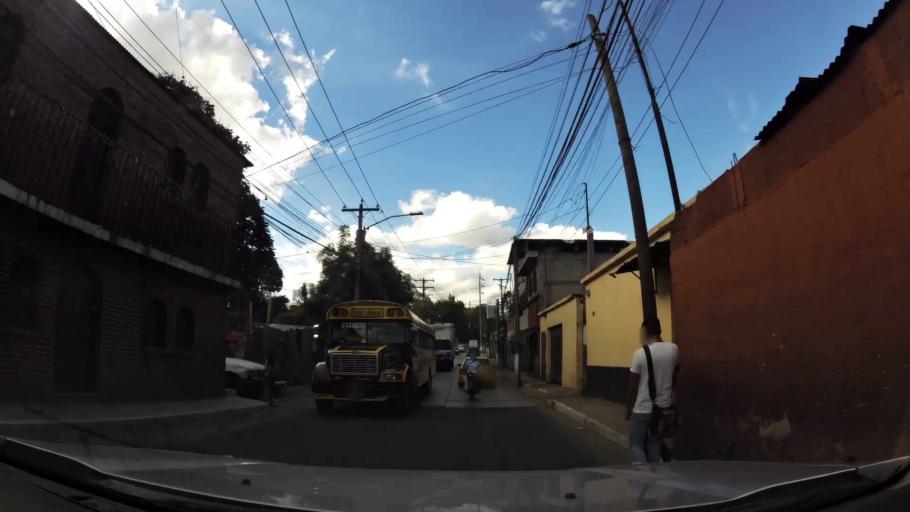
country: GT
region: Guatemala
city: Villa Nueva
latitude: 14.5276
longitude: -90.5938
